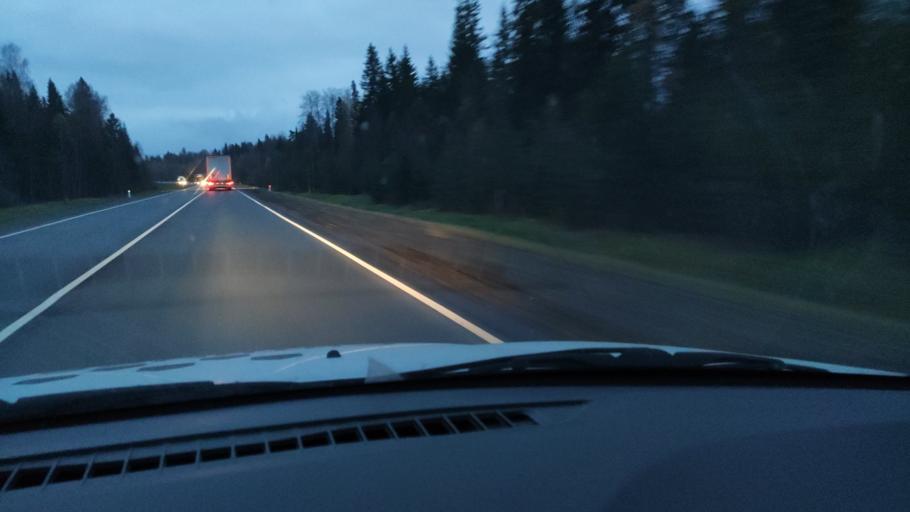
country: RU
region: Kirov
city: Kostino
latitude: 58.8277
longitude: 53.4186
